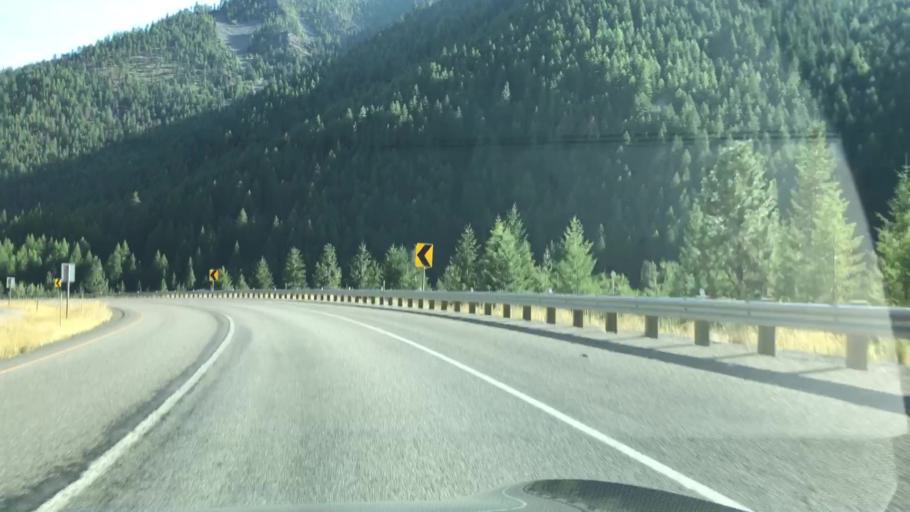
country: US
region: Montana
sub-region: Sanders County
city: Thompson Falls
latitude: 47.3363
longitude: -115.2704
